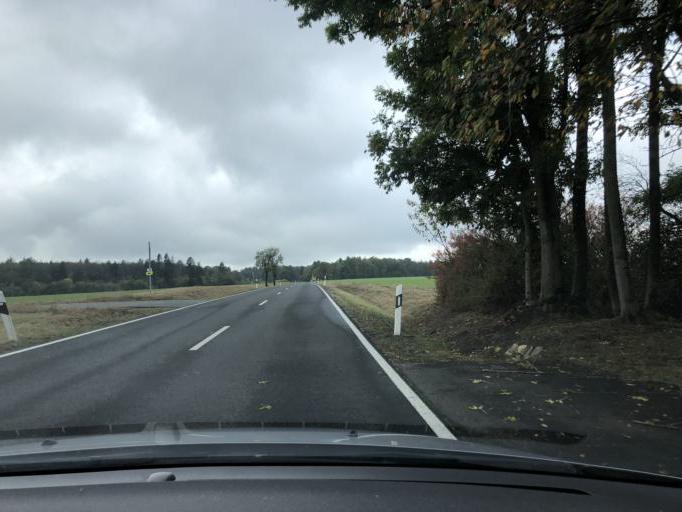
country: DE
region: Thuringia
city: Wachstedt
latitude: 51.2910
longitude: 10.2400
